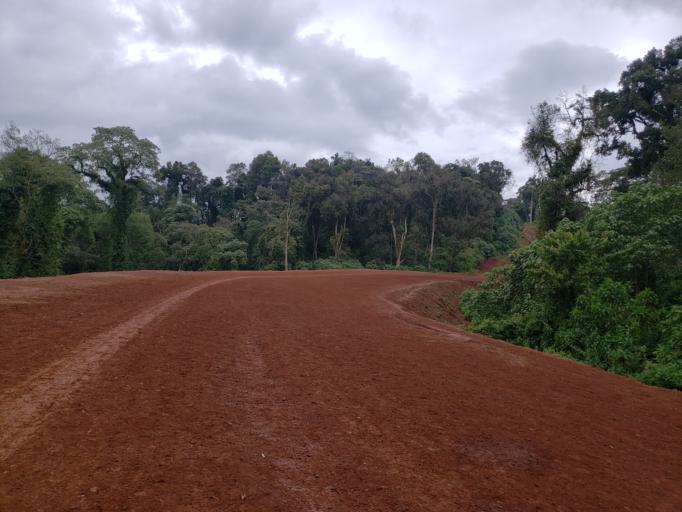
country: ET
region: Oromiya
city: Dodola
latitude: 6.5809
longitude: 39.4182
